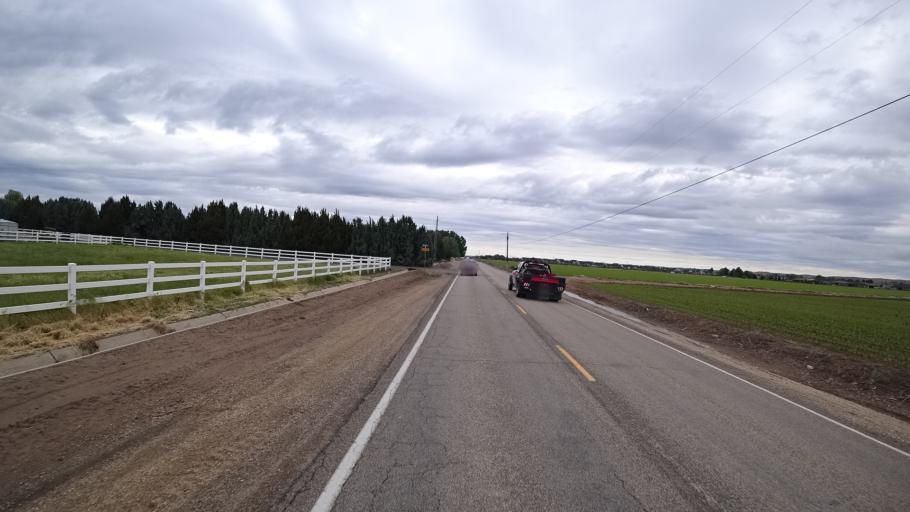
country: US
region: Idaho
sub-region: Ada County
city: Eagle
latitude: 43.7062
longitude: -116.4081
